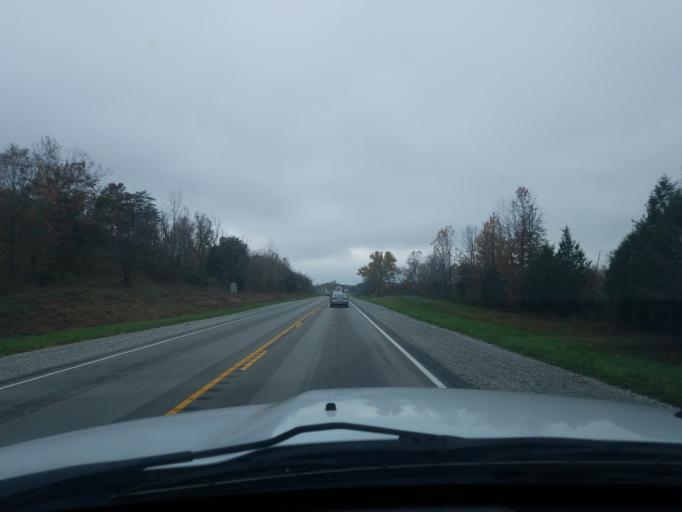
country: US
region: Kentucky
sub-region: Marion County
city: Lebanon
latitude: 37.5278
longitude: -85.3025
